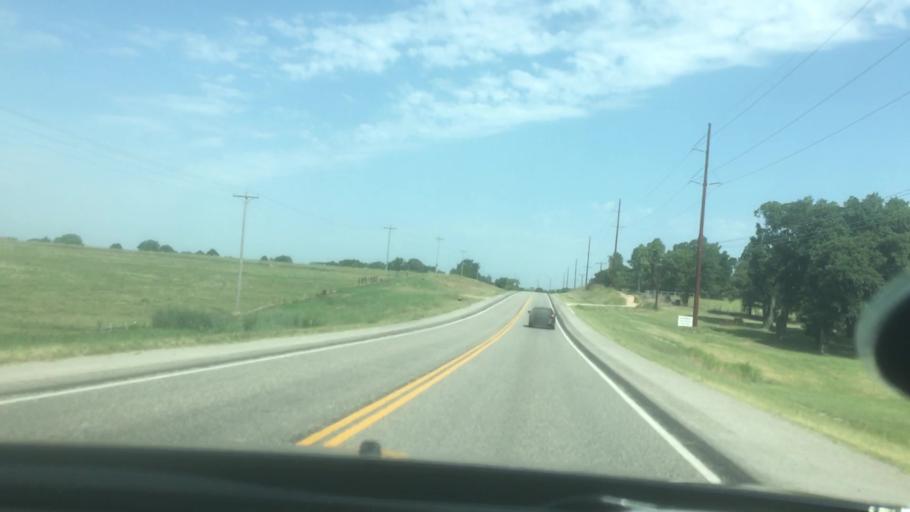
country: US
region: Oklahoma
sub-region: Seminole County
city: Konawa
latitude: 34.8568
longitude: -96.8192
